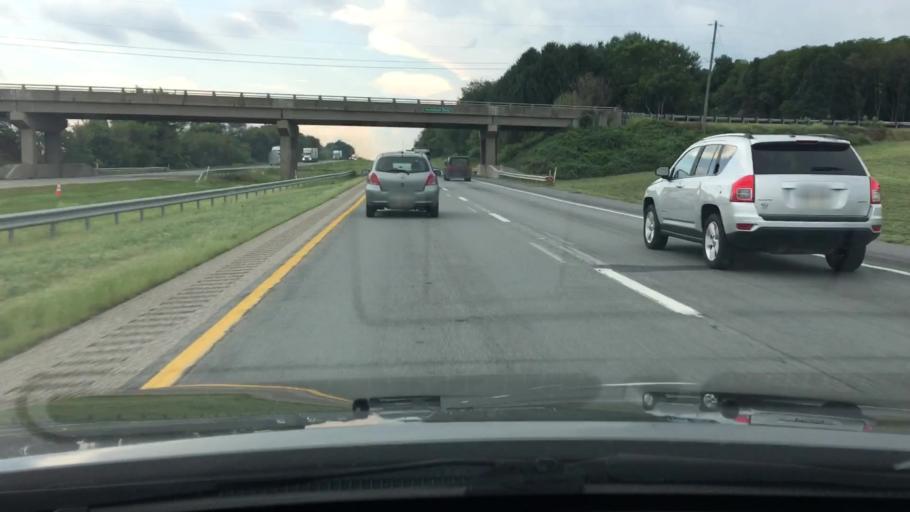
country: US
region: Pennsylvania
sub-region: Cumberland County
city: Newville
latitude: 40.0845
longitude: -77.4294
